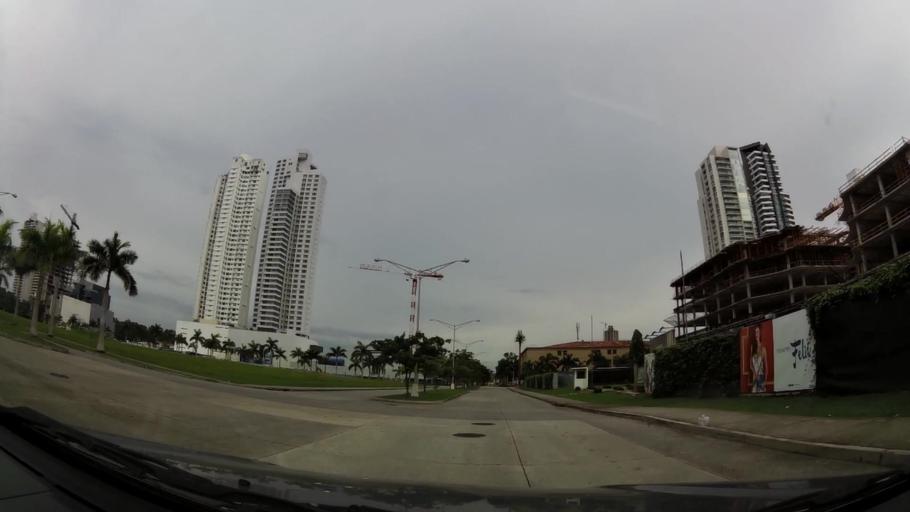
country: PA
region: Panama
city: San Miguelito
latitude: 9.0144
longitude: -79.4658
